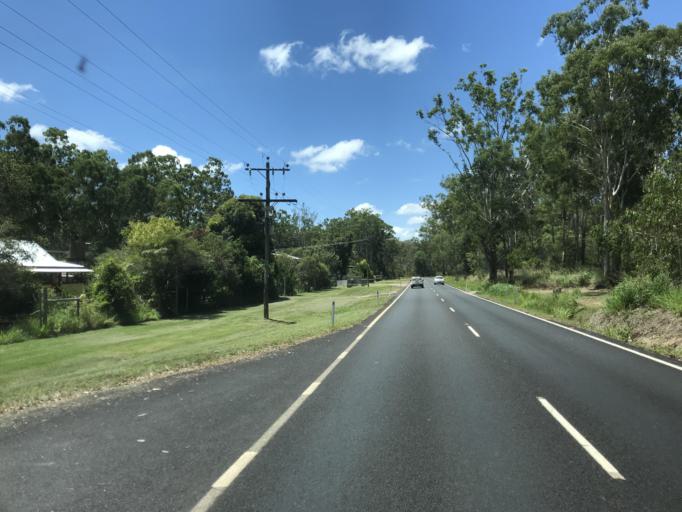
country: AU
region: Queensland
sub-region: Tablelands
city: Atherton
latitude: -17.4083
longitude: 145.3906
